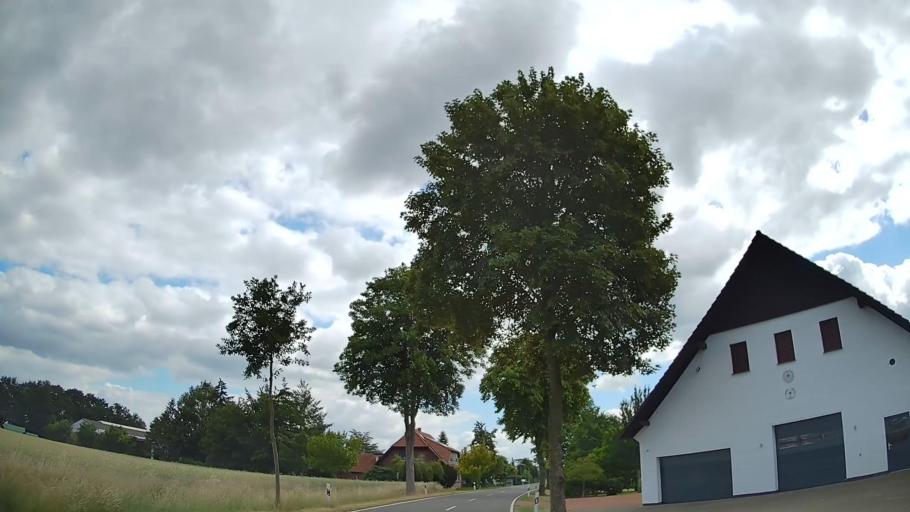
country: DE
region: Lower Saxony
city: Brockum
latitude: 52.4519
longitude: 8.4881
